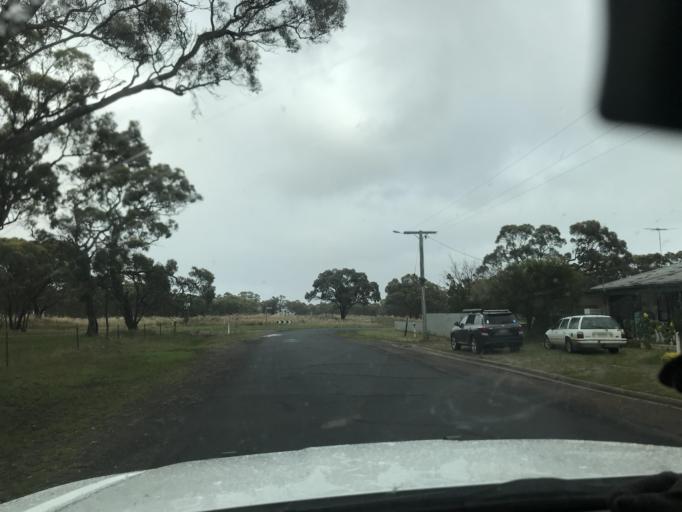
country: AU
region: Victoria
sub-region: Horsham
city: Horsham
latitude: -36.7227
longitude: 141.4724
